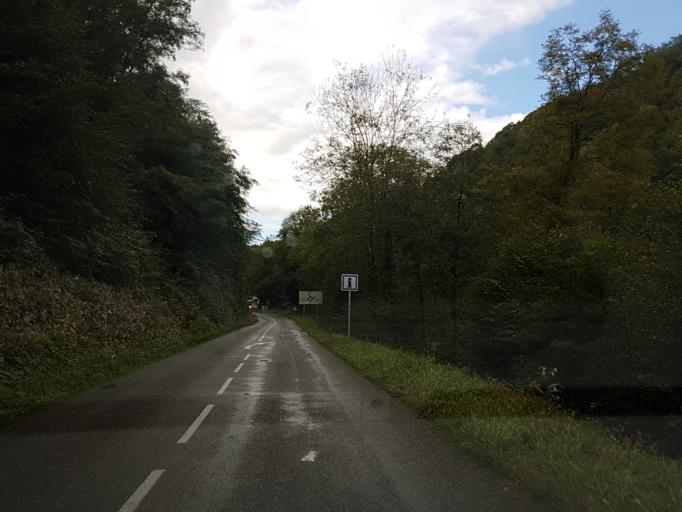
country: FR
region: Midi-Pyrenees
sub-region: Departement de l'Ariege
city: Saint-Girons
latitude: 42.9079
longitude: 1.2173
